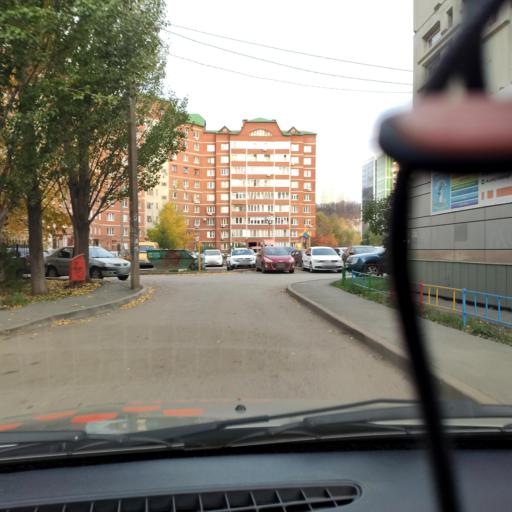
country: RU
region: Bashkortostan
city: Ufa
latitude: 54.7631
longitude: 56.0495
